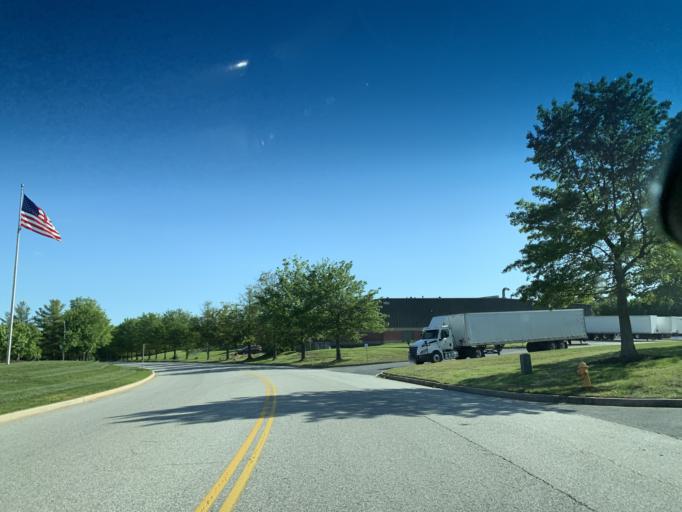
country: US
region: Maryland
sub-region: Harford County
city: Riverside
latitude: 39.4845
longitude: -76.2349
